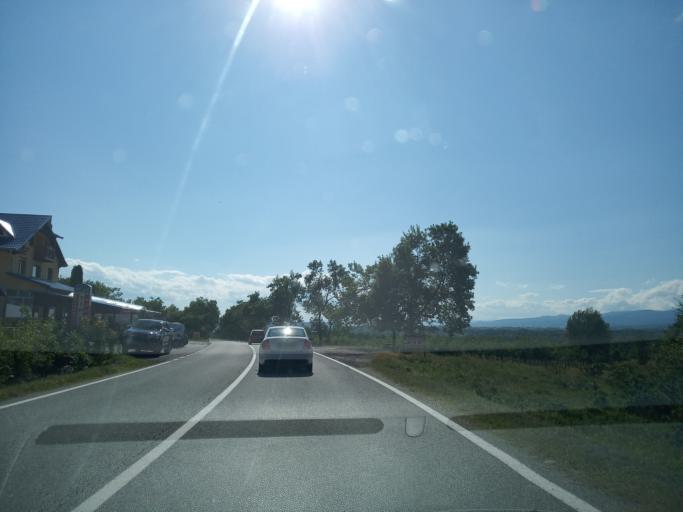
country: RO
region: Gorj
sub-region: Comuna Baia de Fier
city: Baia de Fier
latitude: 45.1431
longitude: 23.7657
